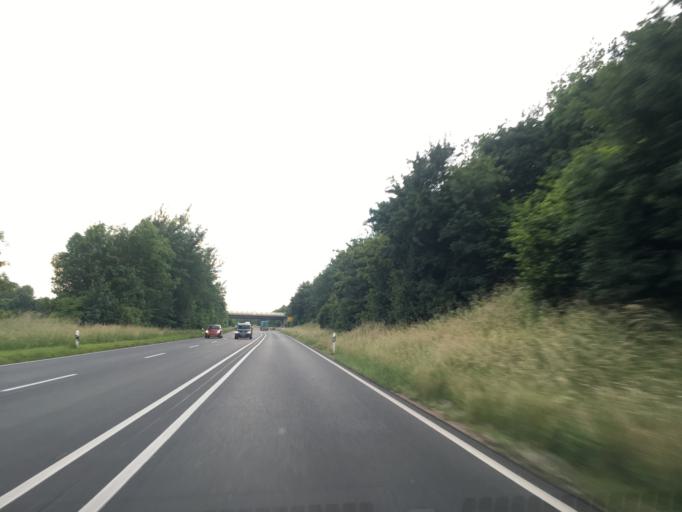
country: DE
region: North Rhine-Westphalia
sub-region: Regierungsbezirk Munster
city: Ochtrup
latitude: 52.1953
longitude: 7.1664
